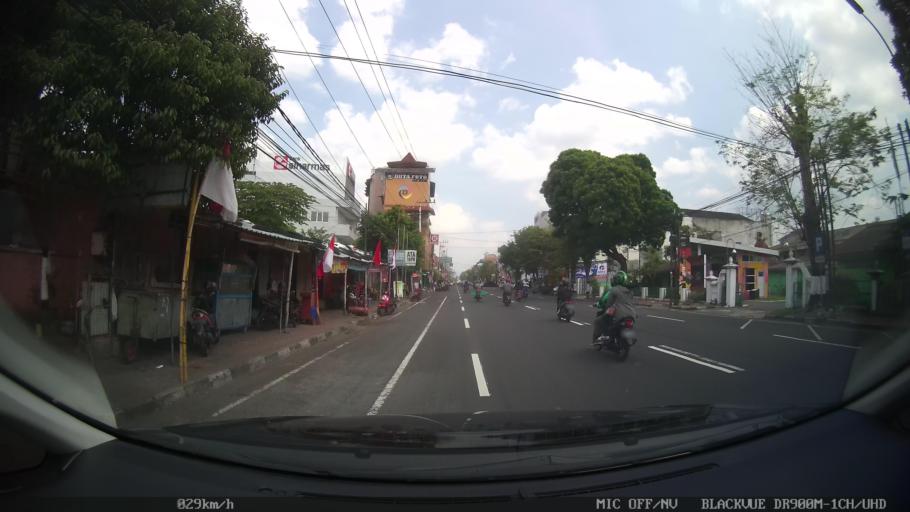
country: ID
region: Daerah Istimewa Yogyakarta
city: Yogyakarta
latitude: -7.7832
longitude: 110.3842
